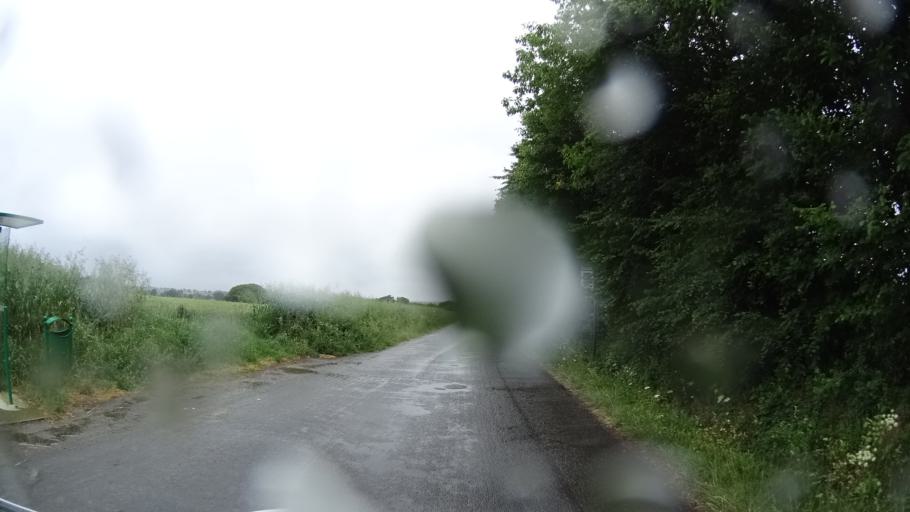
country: FR
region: Brittany
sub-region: Departement d'Ille-et-Vilaine
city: Saint-Erblon
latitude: 48.0205
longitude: -1.6319
